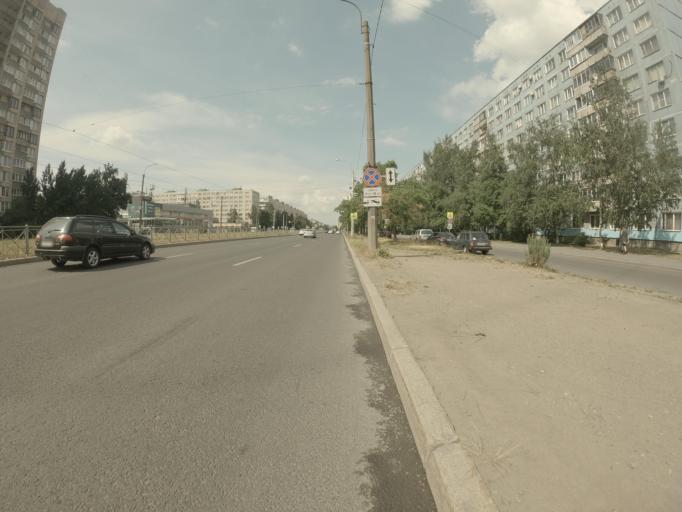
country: RU
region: St.-Petersburg
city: Krasnogvargeisky
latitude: 59.9200
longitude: 30.4940
